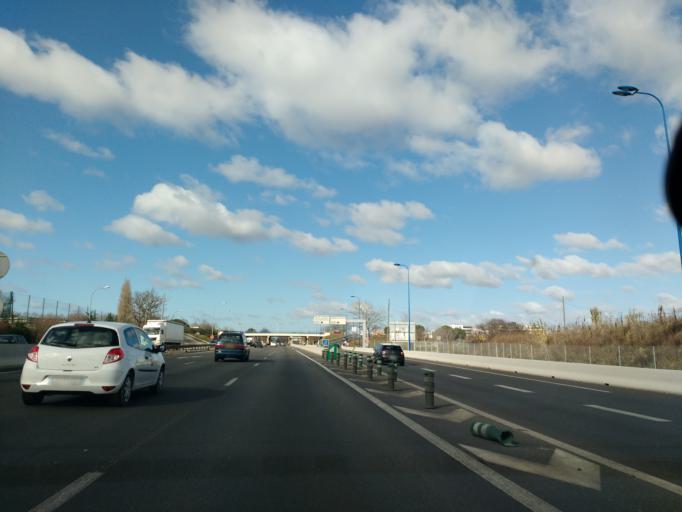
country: FR
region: Midi-Pyrenees
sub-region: Departement de la Haute-Garonne
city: Ramonville-Saint-Agne
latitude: 43.5698
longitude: 1.4781
